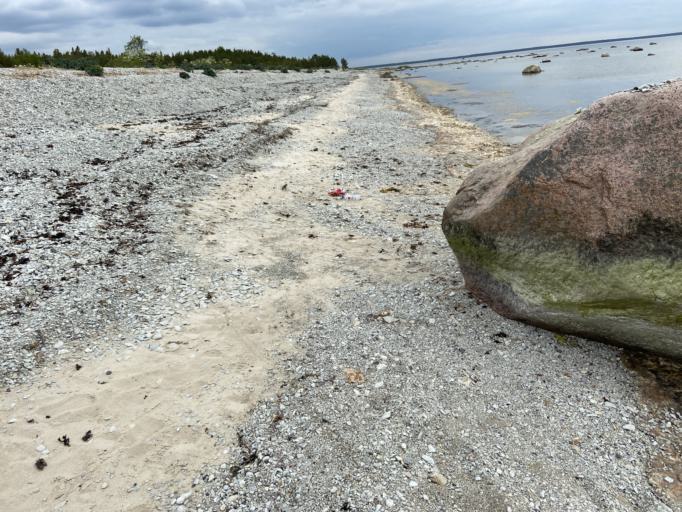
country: EE
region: Harju
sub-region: Paldiski linn
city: Paldiski
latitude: 59.2694
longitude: 23.7315
